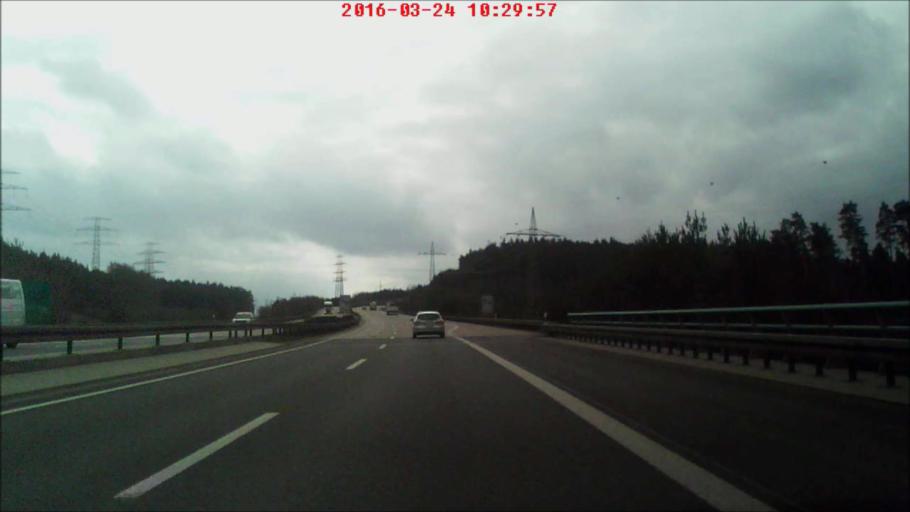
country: DE
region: Thuringia
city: Behringen
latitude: 50.7691
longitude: 11.0028
